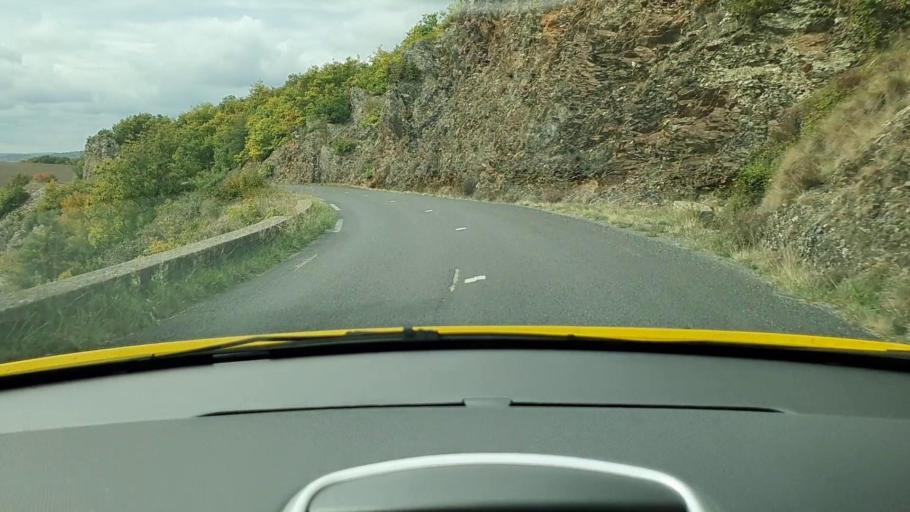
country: FR
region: Languedoc-Roussillon
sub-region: Departement de la Lozere
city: Meyrueis
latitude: 44.0639
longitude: 3.4036
